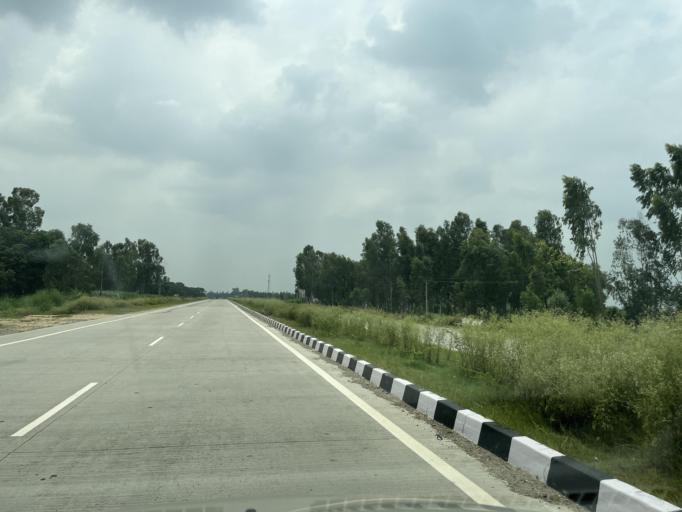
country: IN
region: Uttar Pradesh
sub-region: Bijnor
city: Najibabad
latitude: 29.5563
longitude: 78.3391
